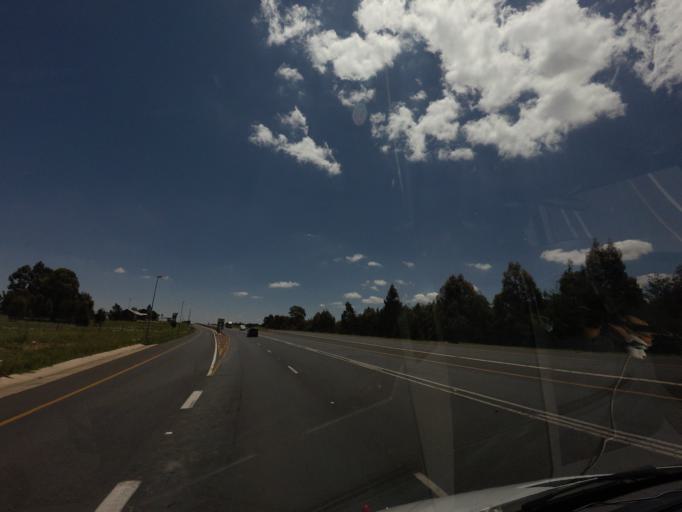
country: ZA
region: Mpumalanga
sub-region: Nkangala District Municipality
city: Belfast
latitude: -25.7137
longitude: 30.0612
